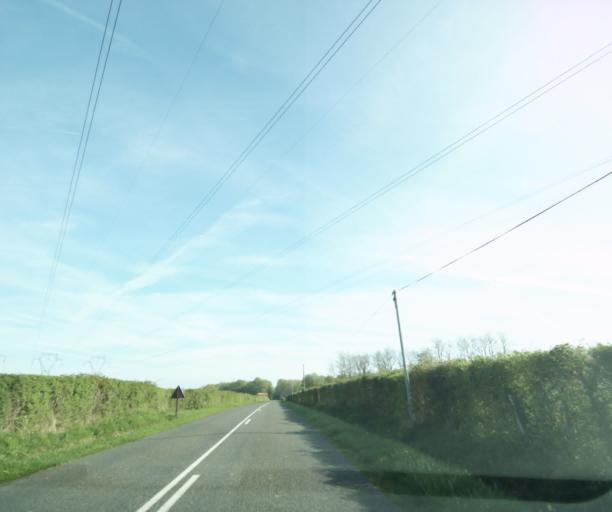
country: FR
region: Ile-de-France
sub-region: Departement de Seine-et-Marne
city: Vernou-la-Celle-sur-Seine
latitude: 48.4396
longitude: 2.8559
